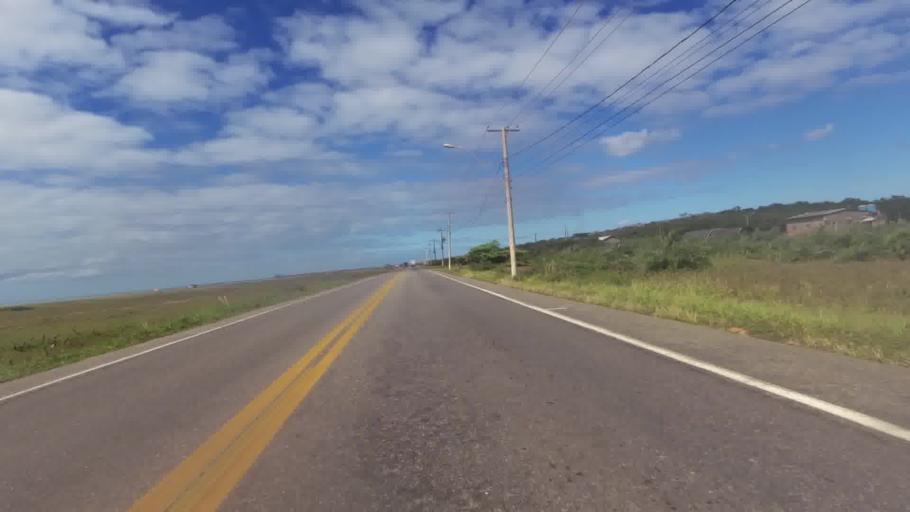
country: BR
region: Espirito Santo
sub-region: Itapemirim
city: Itapemirim
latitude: -20.9648
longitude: -40.8103
